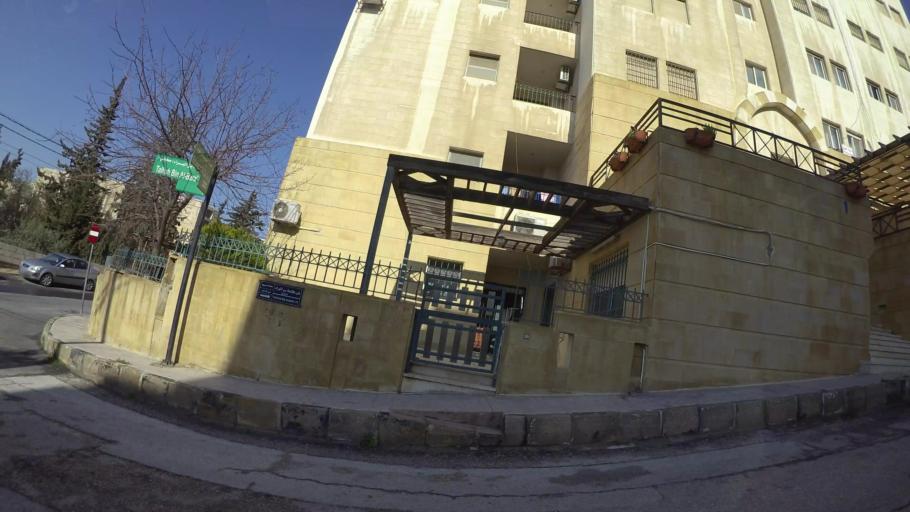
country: JO
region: Amman
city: Al Jubayhah
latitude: 31.9941
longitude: 35.8890
